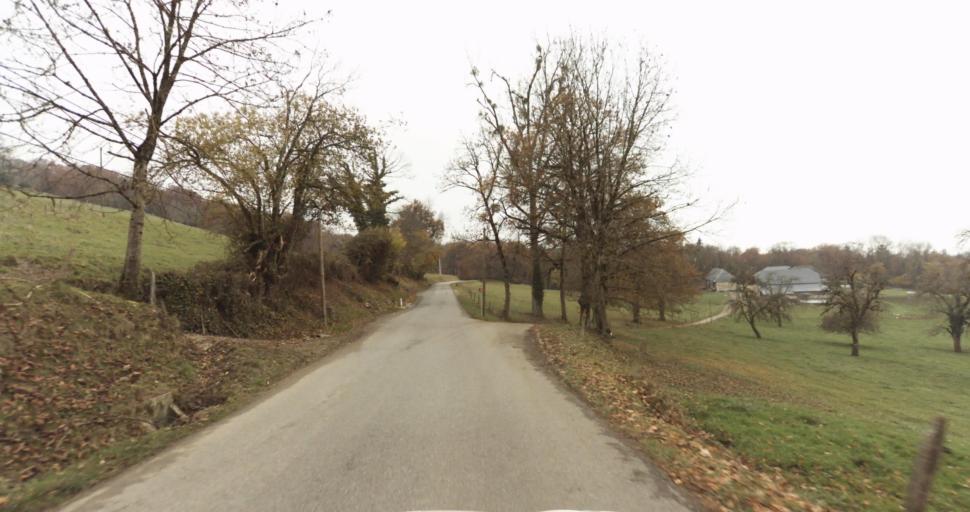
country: FR
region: Rhone-Alpes
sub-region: Departement de la Haute-Savoie
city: Cusy
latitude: 45.7569
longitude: 6.0189
